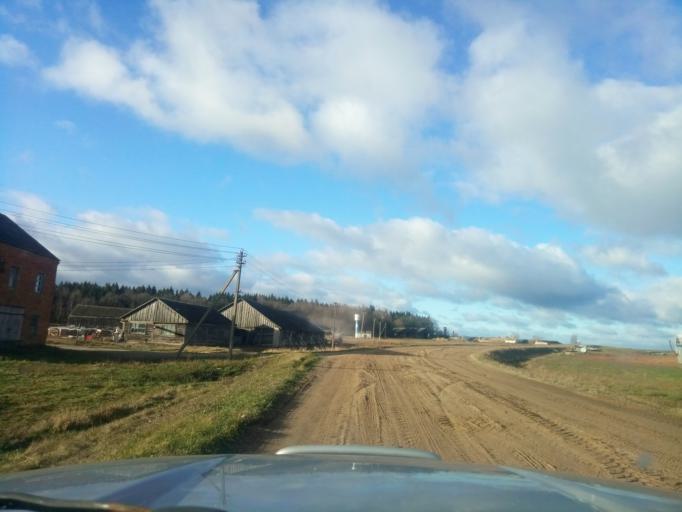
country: BY
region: Minsk
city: Tsimkavichy
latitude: 53.1803
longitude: 26.9511
